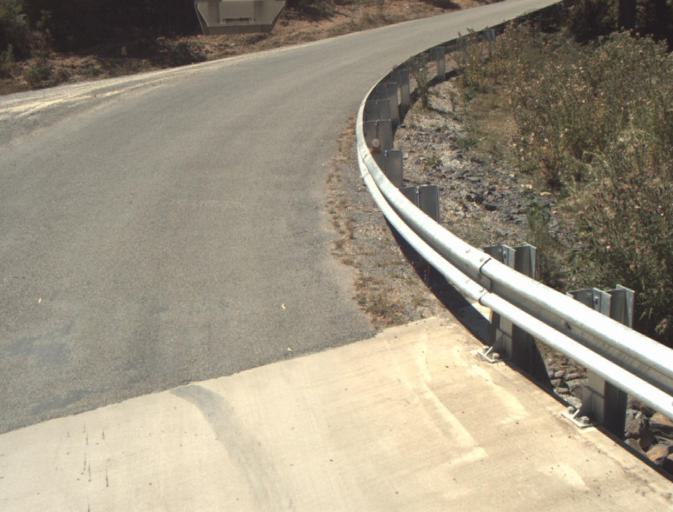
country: AU
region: Tasmania
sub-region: Dorset
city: Scottsdale
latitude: -41.2935
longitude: 147.4073
